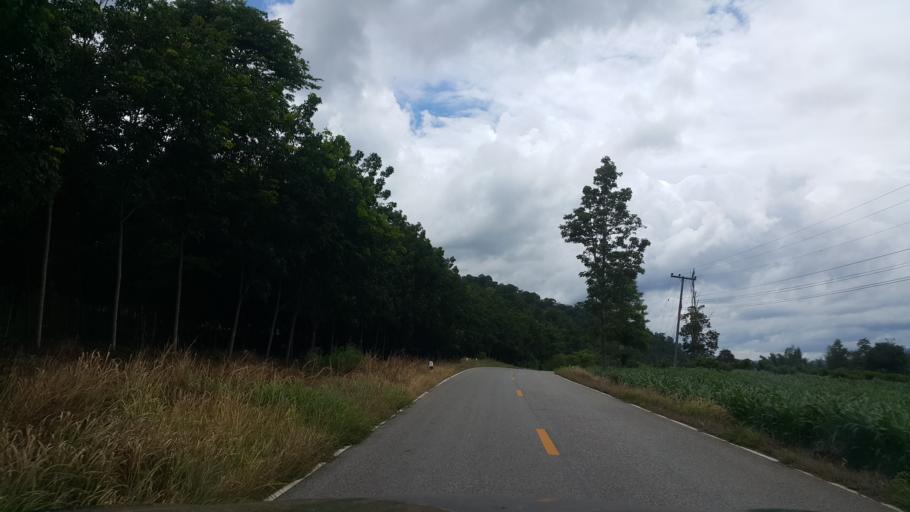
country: TH
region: Phitsanulok
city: Chat Trakan
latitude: 17.4000
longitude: 100.7620
